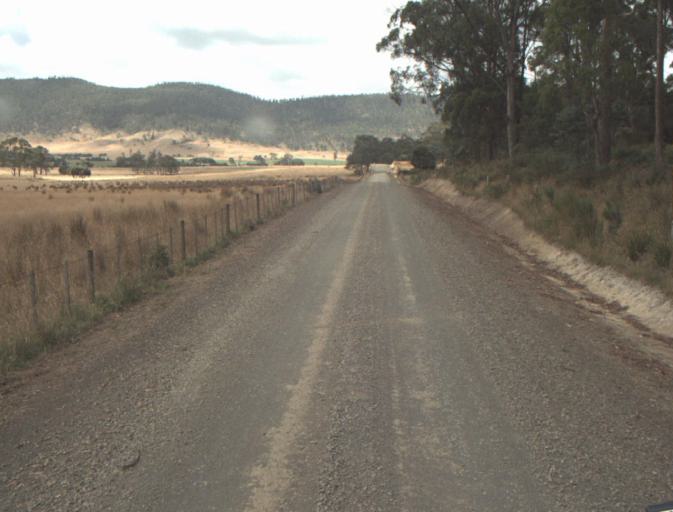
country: AU
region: Tasmania
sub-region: Northern Midlands
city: Evandale
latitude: -41.4643
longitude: 147.4487
